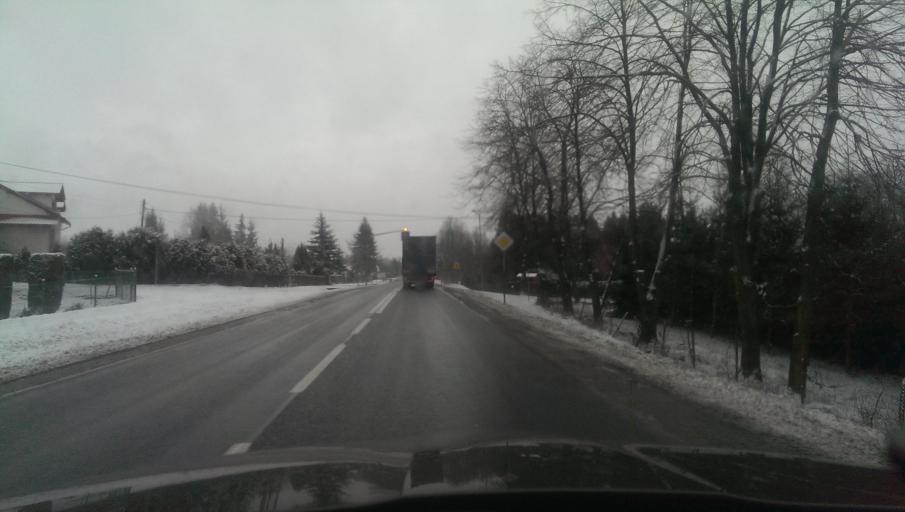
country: PL
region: Subcarpathian Voivodeship
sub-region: Powiat sanocki
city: Nowosielce-Gniewosz
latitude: 49.5704
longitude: 22.0665
